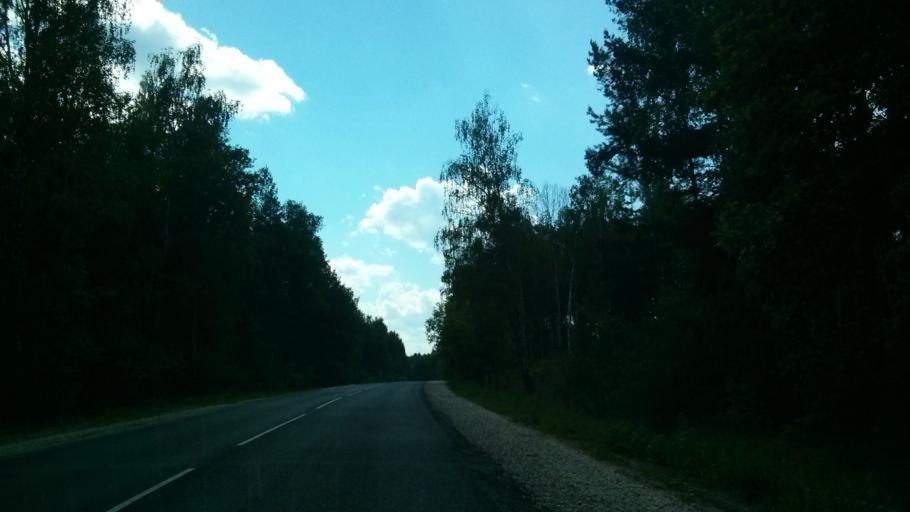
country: RU
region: Vladimir
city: Murom
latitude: 55.5076
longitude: 41.9193
